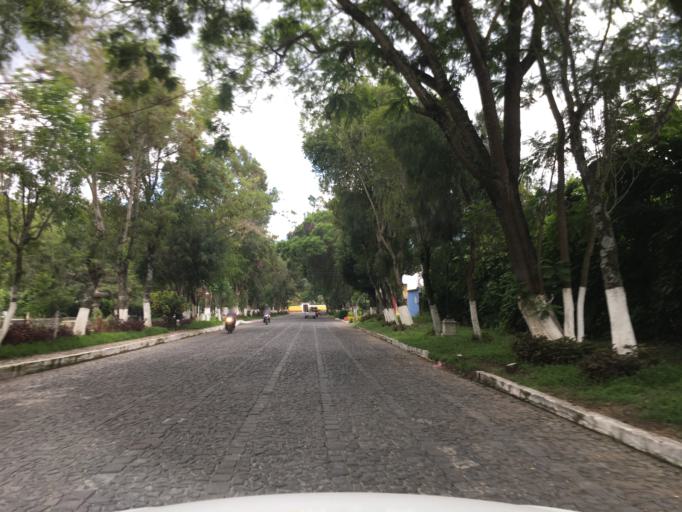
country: GT
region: Sacatepequez
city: Antigua Guatemala
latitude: 14.5477
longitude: -90.7301
